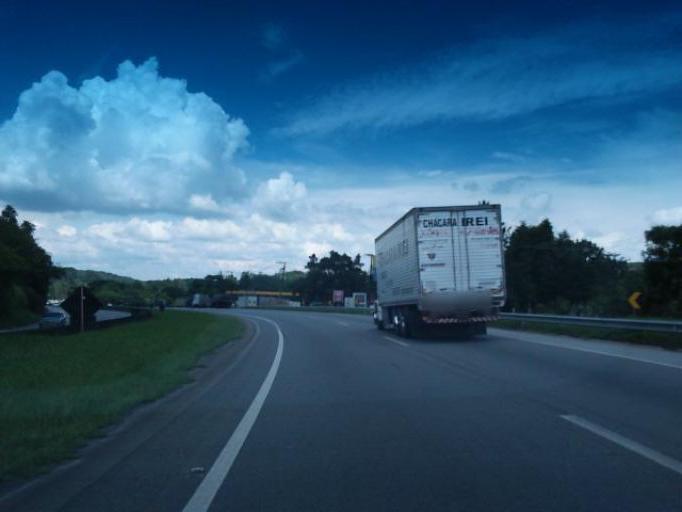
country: BR
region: Sao Paulo
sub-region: Juquitiba
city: Juquitiba
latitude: -23.9350
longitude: -47.0328
